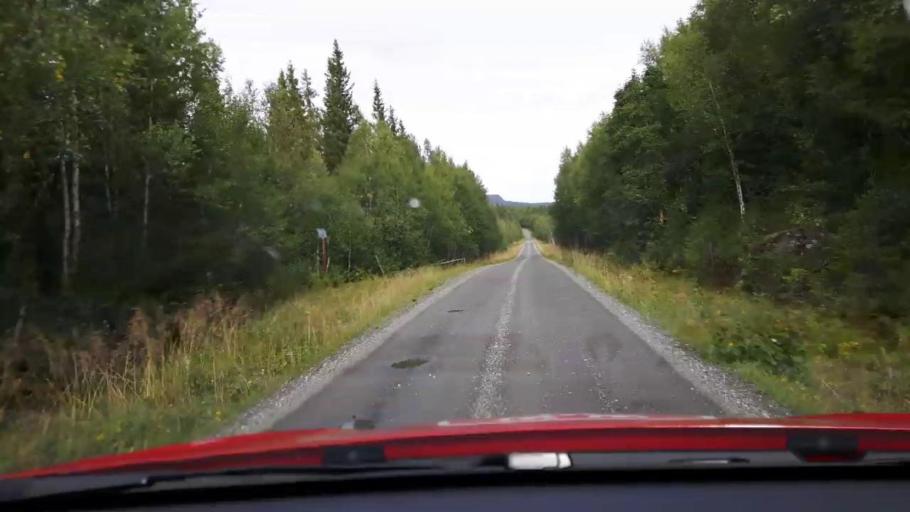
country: SE
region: Jaemtland
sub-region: Are Kommun
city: Are
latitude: 63.7792
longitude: 13.0995
